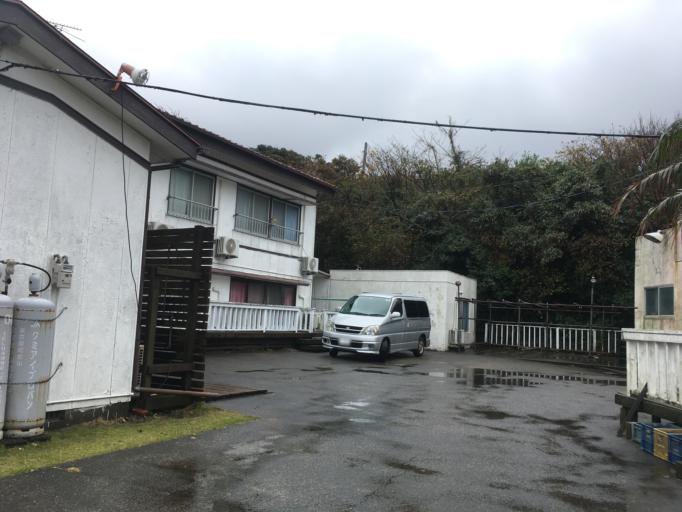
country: JP
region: Shizuoka
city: Ito
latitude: 34.7793
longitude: 139.3547
